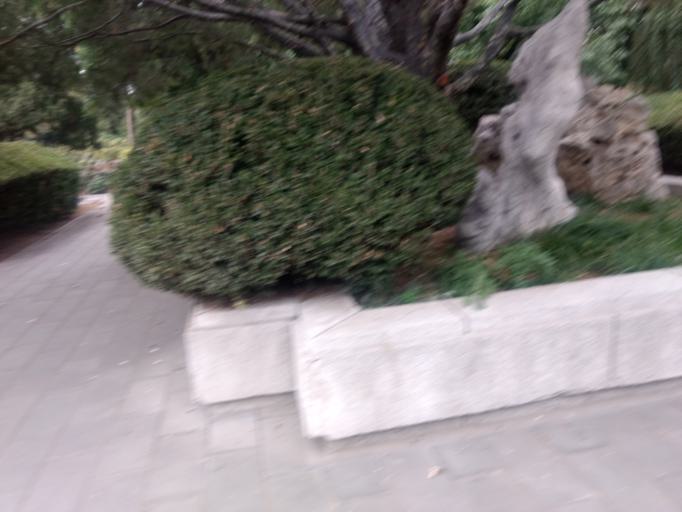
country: CN
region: Beijing
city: Longtan
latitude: 39.8815
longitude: 116.4018
